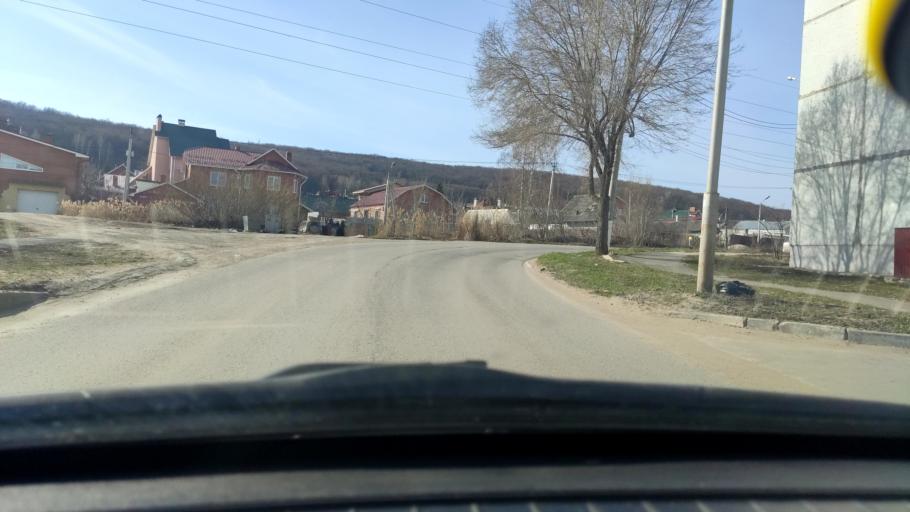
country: RU
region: Samara
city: Zhigulevsk
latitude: 53.3950
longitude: 49.4974
